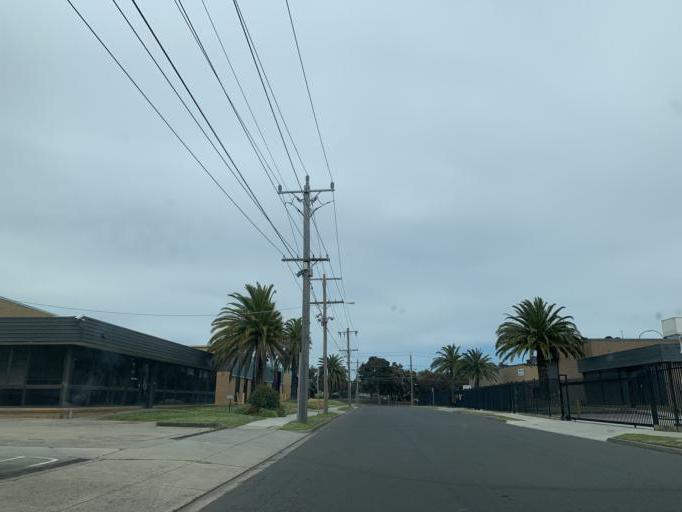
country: AU
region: Victoria
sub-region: Bayside
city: Highett
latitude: -37.9567
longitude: 145.0315
